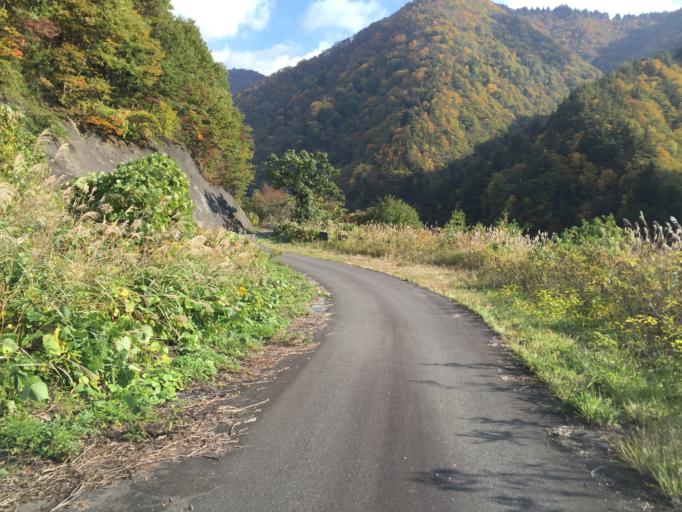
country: JP
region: Fukushima
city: Kitakata
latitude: 37.7508
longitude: 139.9190
